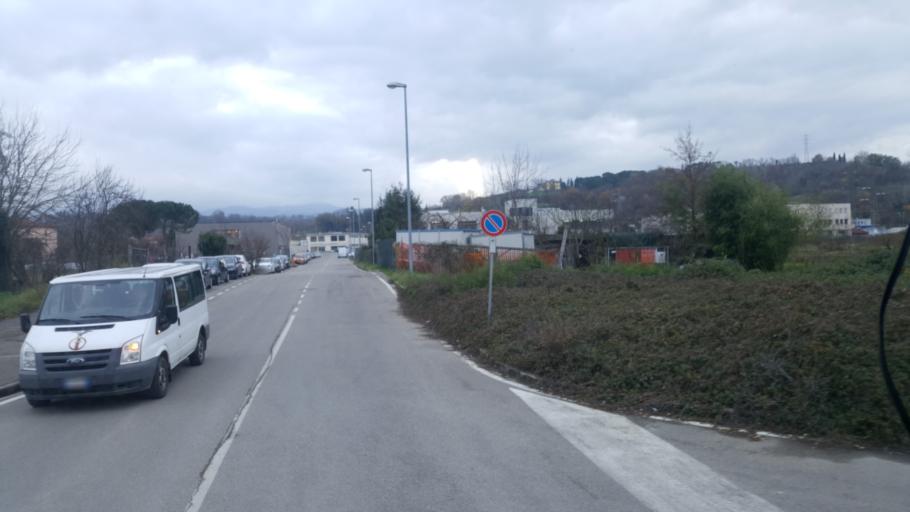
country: IT
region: Tuscany
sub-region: Province of Arezzo
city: Montevarchi
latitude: 43.5391
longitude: 11.5598
